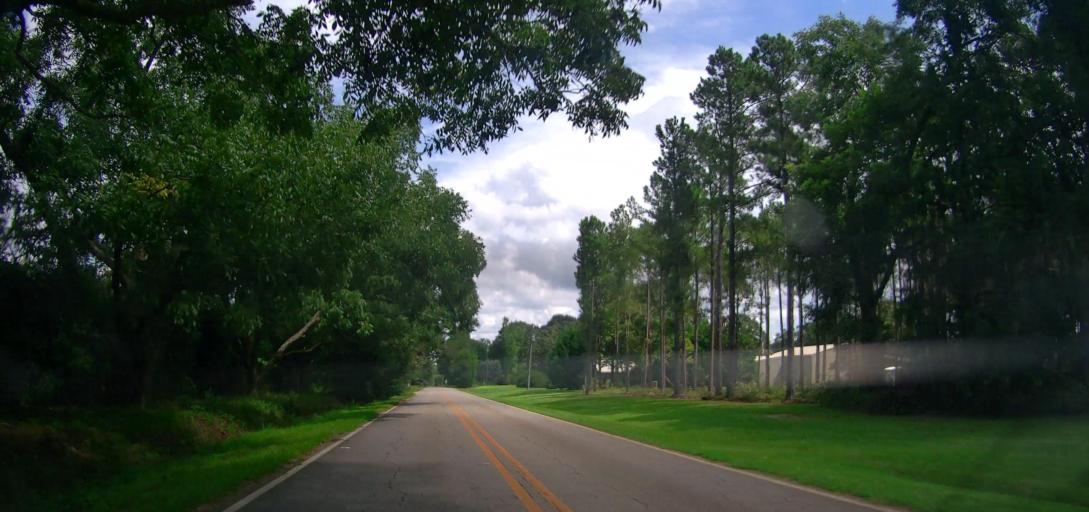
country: US
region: Georgia
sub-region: Houston County
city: Perry
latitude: 32.5222
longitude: -83.7529
